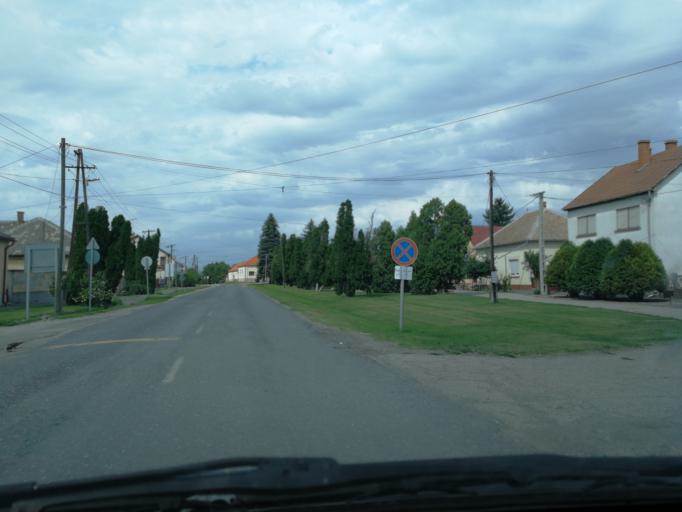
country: HU
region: Bacs-Kiskun
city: Batya
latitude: 46.4472
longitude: 19.0309
